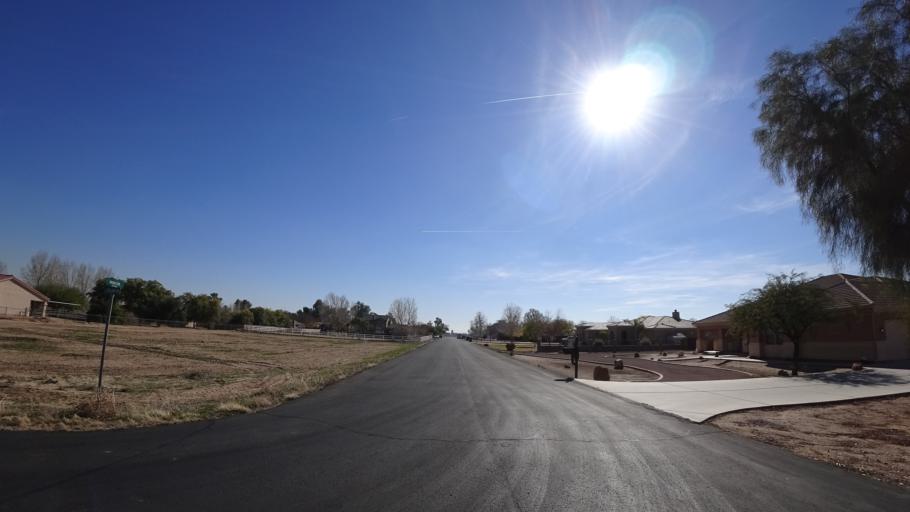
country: US
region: Arizona
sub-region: Maricopa County
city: Citrus Park
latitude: 33.5071
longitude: -112.4689
